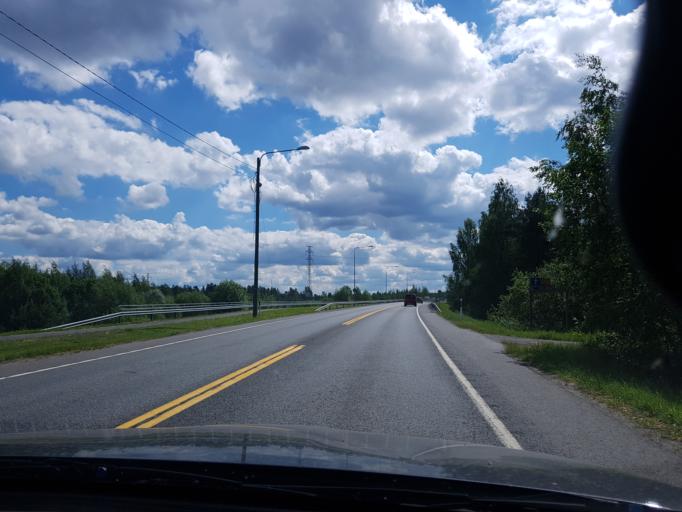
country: FI
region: Haeme
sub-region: Haemeenlinna
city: Haemeenlinna
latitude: 61.0237
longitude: 24.4222
